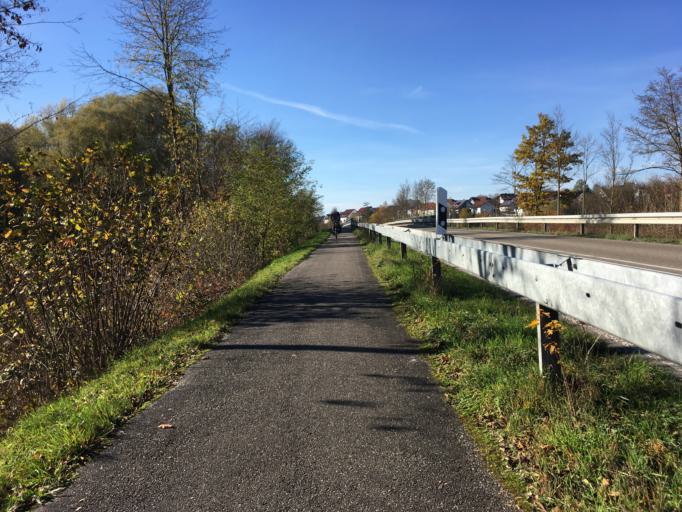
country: DE
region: Baden-Wuerttemberg
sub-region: Karlsruhe Region
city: Zaisenhausen
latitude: 49.1123
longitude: 8.8295
